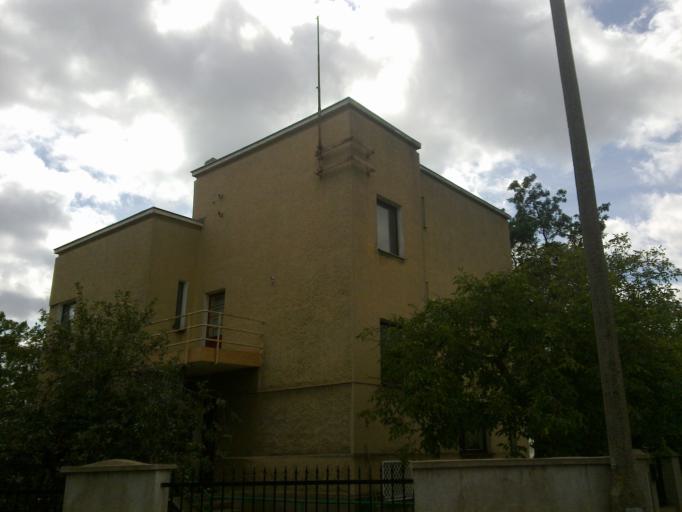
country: PL
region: Pomeranian Voivodeship
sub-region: Gdynia
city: Gdynia
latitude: 54.5119
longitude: 18.5480
